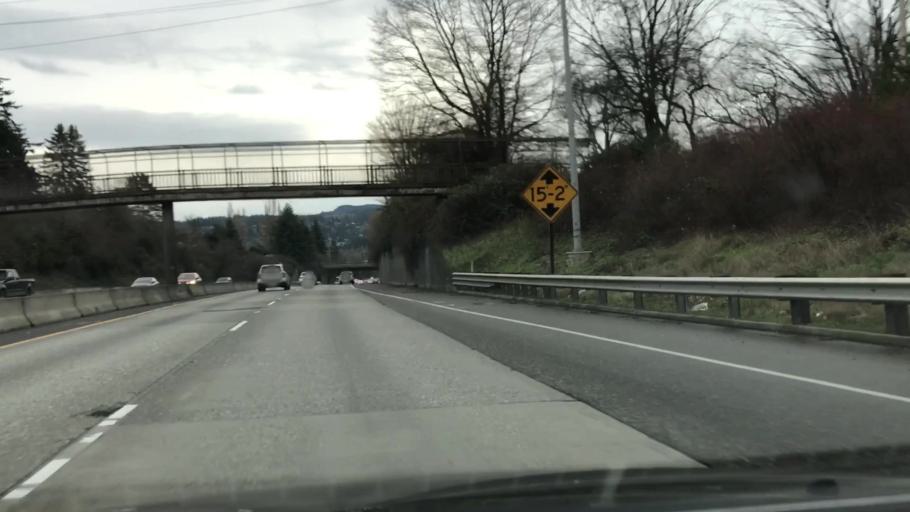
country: US
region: Washington
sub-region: Whatcom County
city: Bellingham
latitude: 48.7683
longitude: -122.4625
